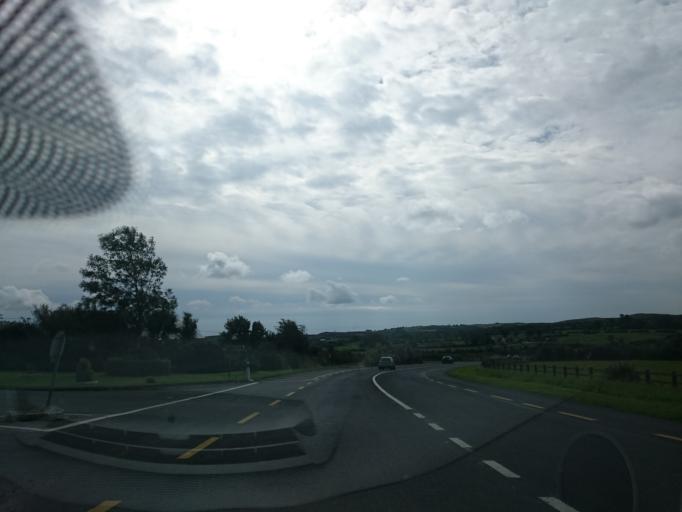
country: IE
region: Munster
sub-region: Waterford
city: Tra Mhor
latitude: 52.1989
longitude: -7.1930
